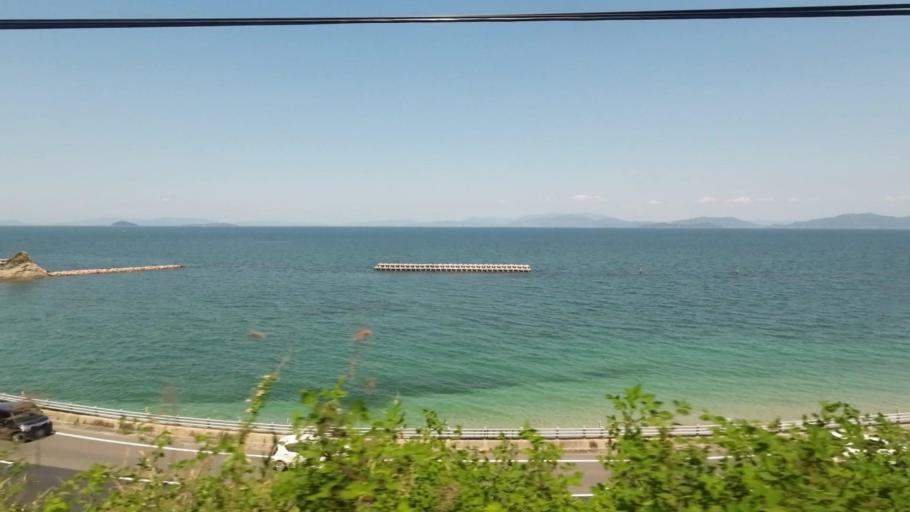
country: JP
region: Ehime
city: Hojo
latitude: 34.0266
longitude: 132.8247
